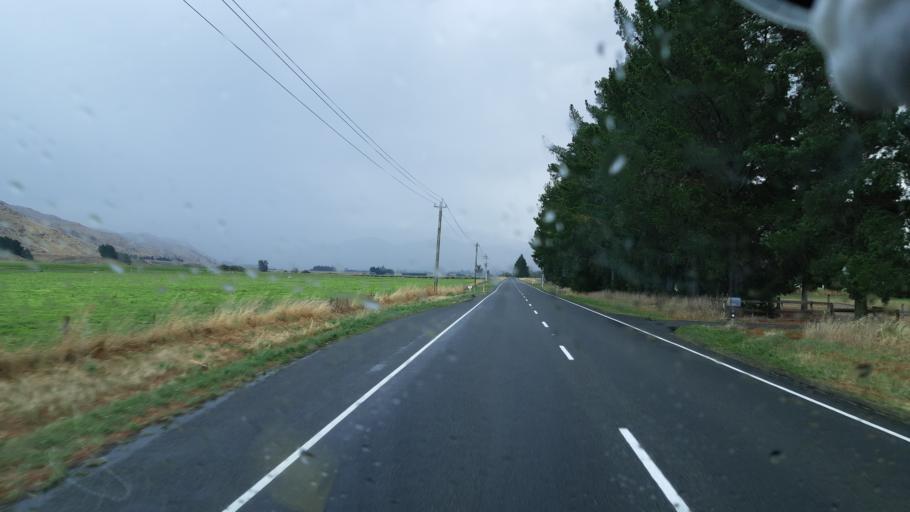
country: NZ
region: Canterbury
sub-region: Hurunui District
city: Amberley
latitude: -42.7112
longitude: 172.8553
